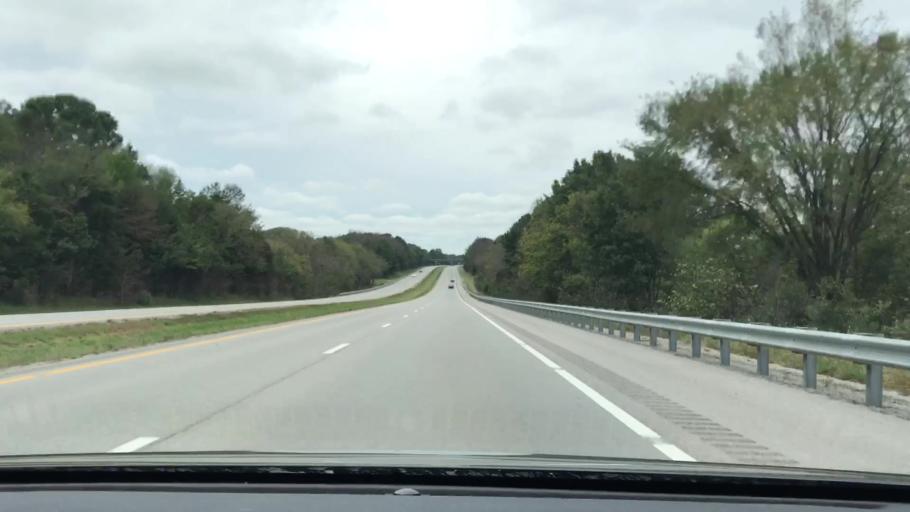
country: US
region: Kentucky
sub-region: Barren County
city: Glasgow
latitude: 37.0089
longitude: -86.0138
